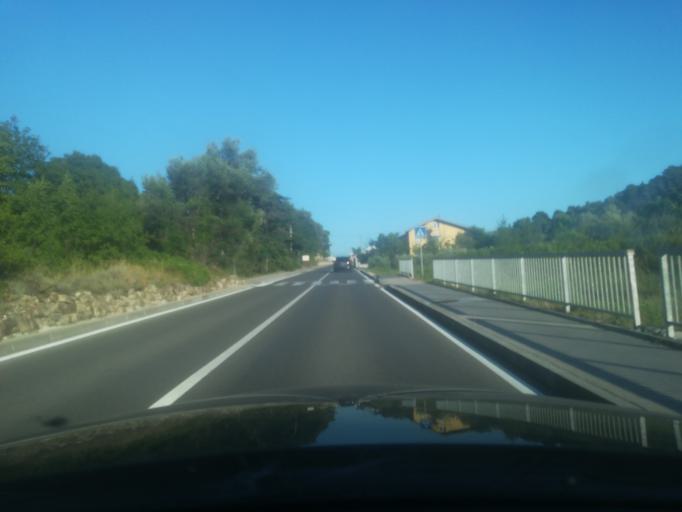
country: HR
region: Primorsko-Goranska
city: Banjol
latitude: 44.7748
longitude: 14.7568
